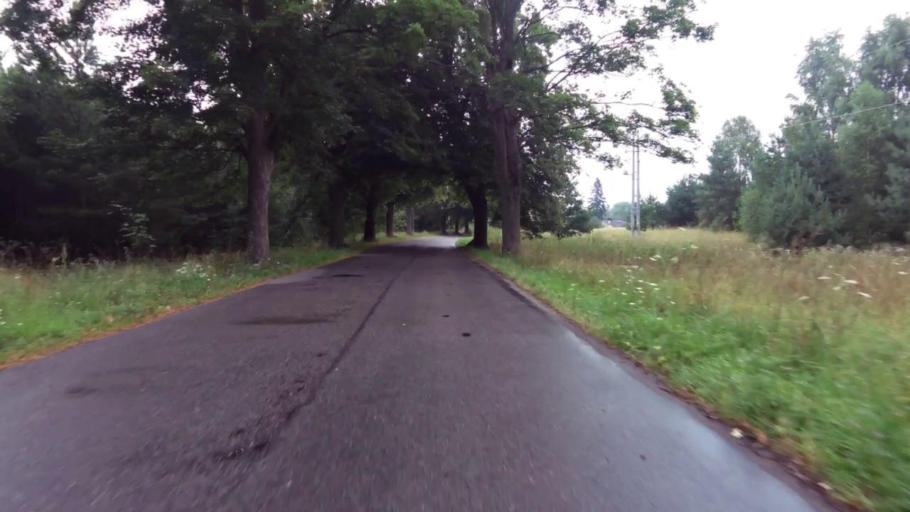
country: PL
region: West Pomeranian Voivodeship
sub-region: Powiat szczecinecki
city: Lubowo
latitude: 53.6072
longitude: 16.3614
